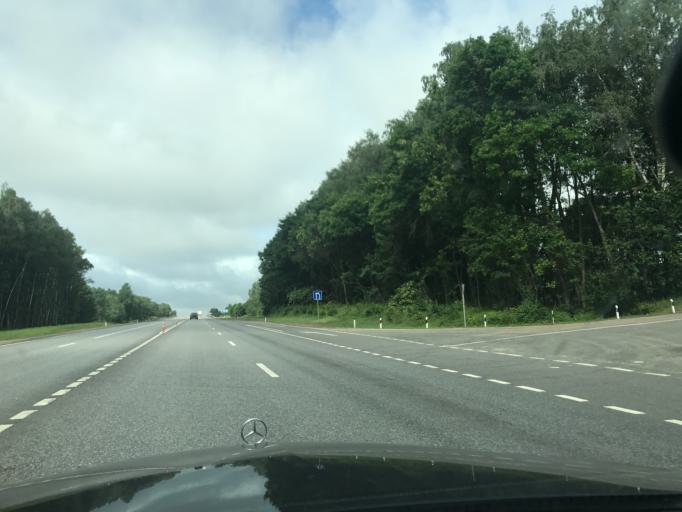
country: RU
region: Smolensk
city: Kardymovo
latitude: 55.0314
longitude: 32.3620
